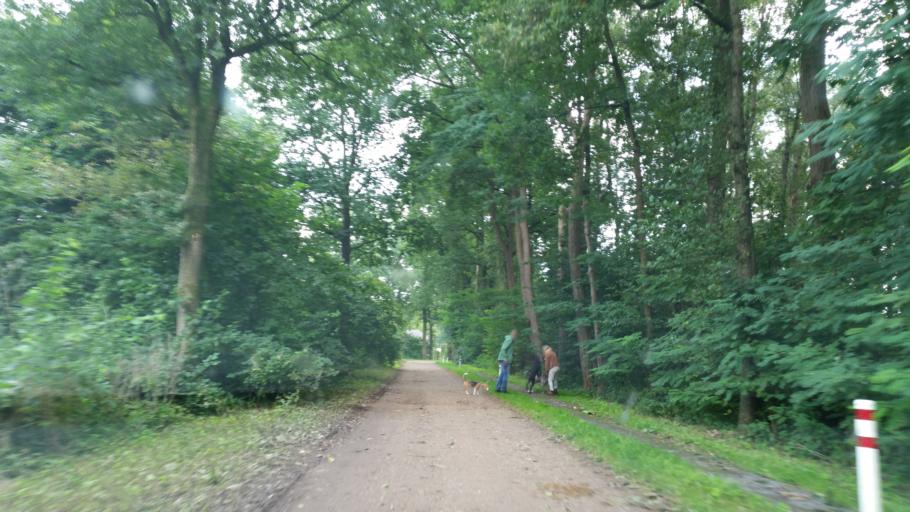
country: NL
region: North Brabant
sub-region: Gemeente Vught
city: Vught
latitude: 51.6372
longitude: 5.2745
